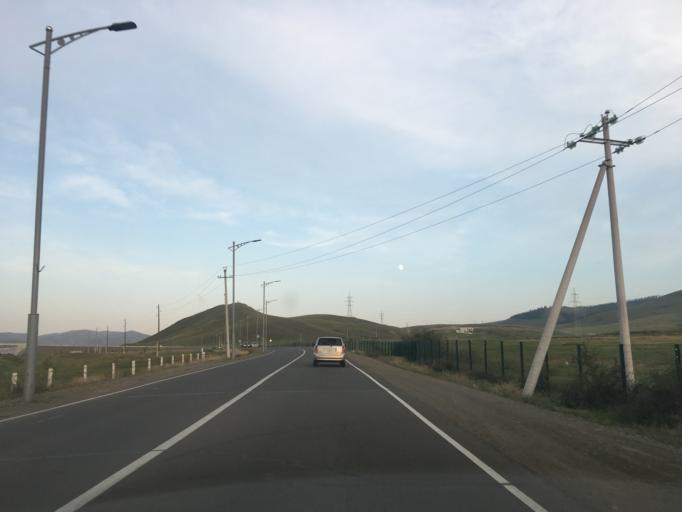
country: MN
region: Ulaanbaatar
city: Ulaanbaatar
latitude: 47.8897
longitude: 107.0432
